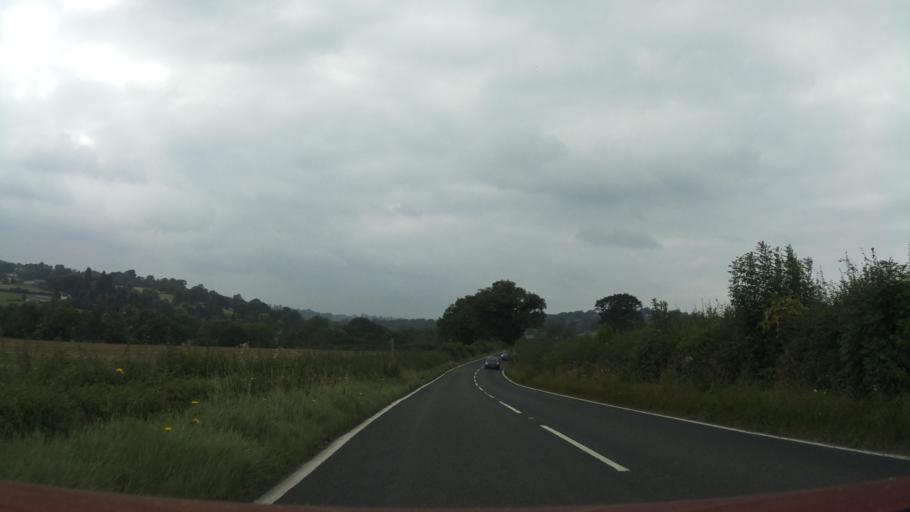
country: GB
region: England
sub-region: Derbyshire
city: Wirksworth
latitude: 53.0249
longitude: -1.5549
